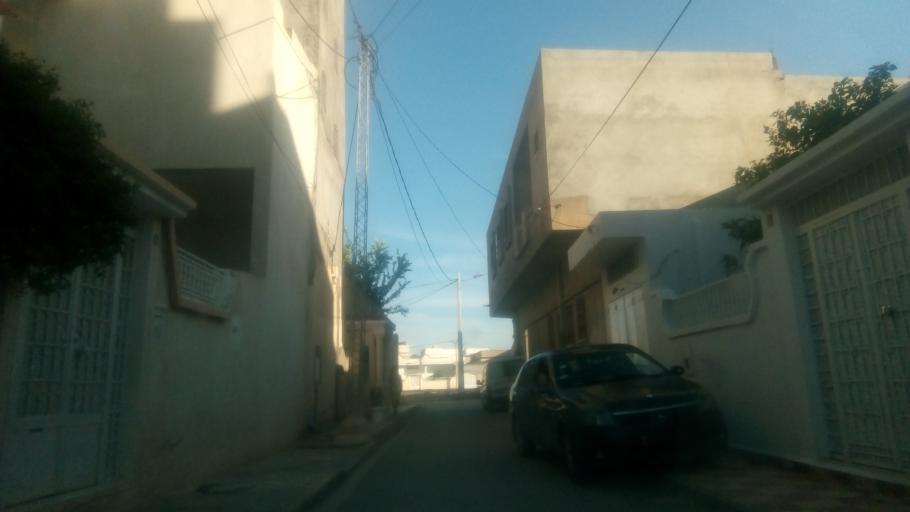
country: TN
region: Al Qayrawan
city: Kairouan
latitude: 35.6683
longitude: 10.0783
